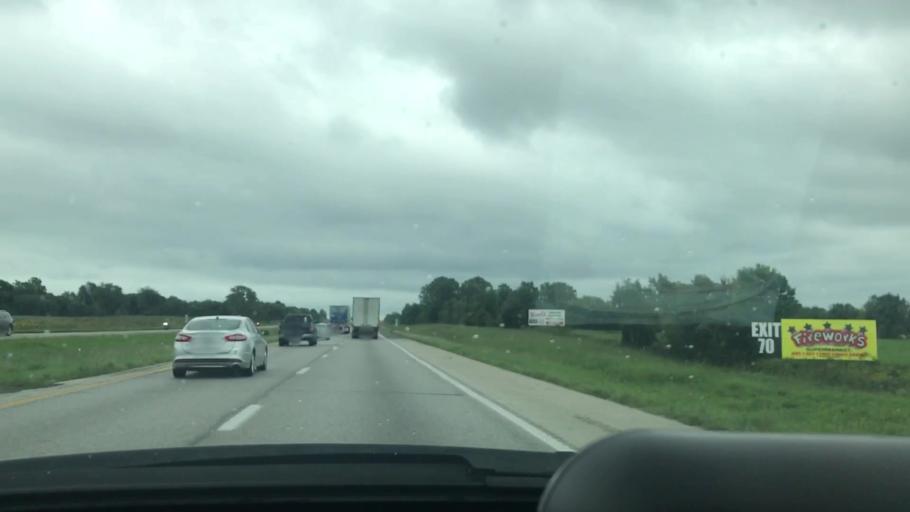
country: US
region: Missouri
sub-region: Greene County
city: Ash Grove
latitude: 37.1865
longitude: -93.6070
